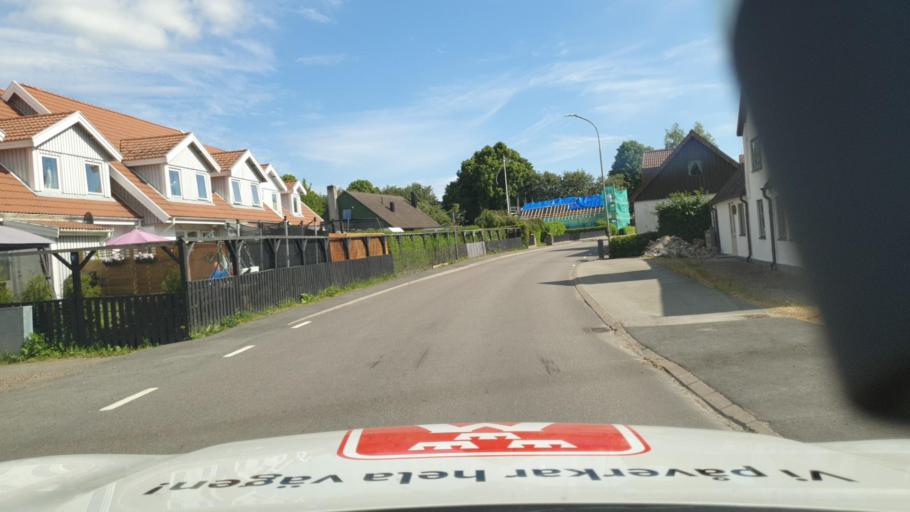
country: SE
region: Skane
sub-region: Skurups Kommun
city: Rydsgard
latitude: 55.5136
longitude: 13.5501
